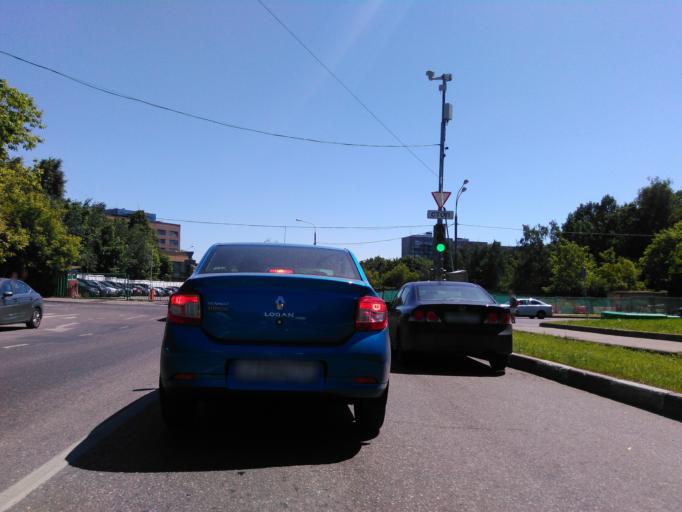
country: RU
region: Moskovskaya
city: Cheremushki
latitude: 55.6461
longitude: 37.5435
